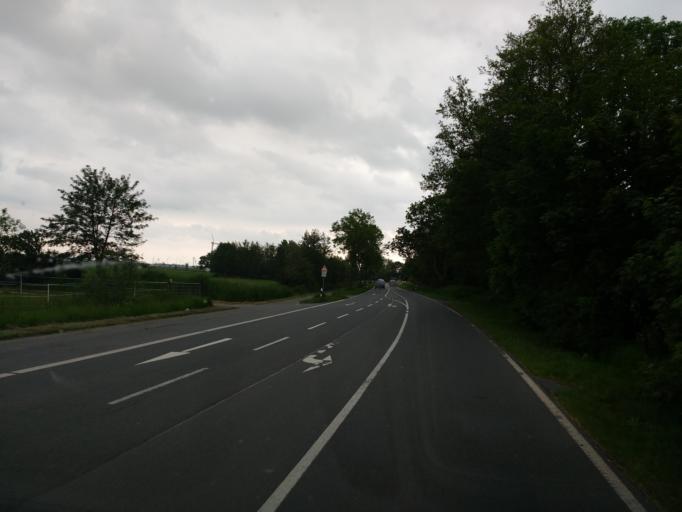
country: DE
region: Lower Saxony
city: Schillig
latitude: 53.6660
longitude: 7.9865
